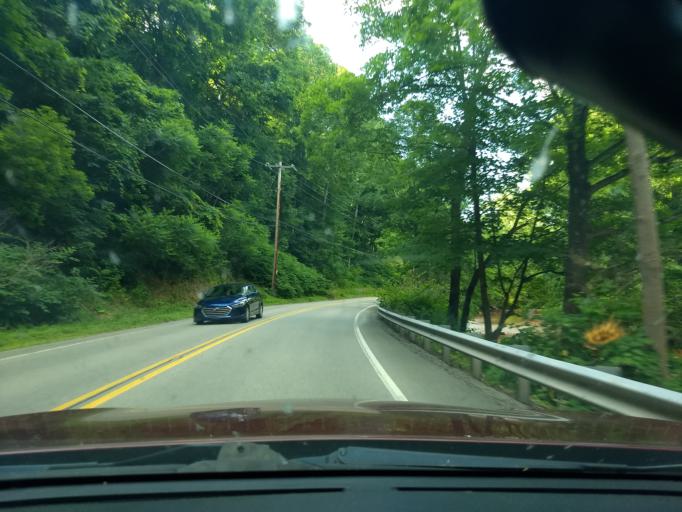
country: US
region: Pennsylvania
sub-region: Westmoreland County
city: Irwin
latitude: 40.3403
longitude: -79.7254
